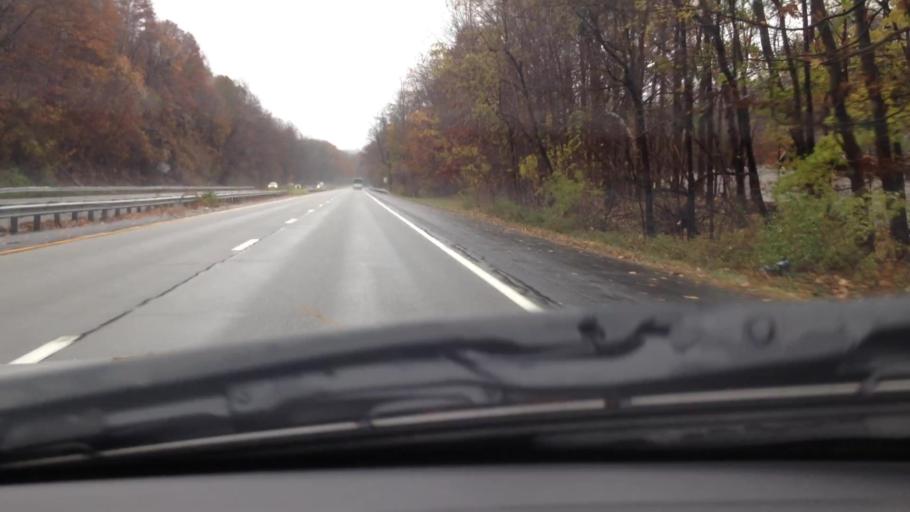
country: US
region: New York
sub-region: Westchester County
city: Crugers
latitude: 41.2414
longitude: -73.9172
